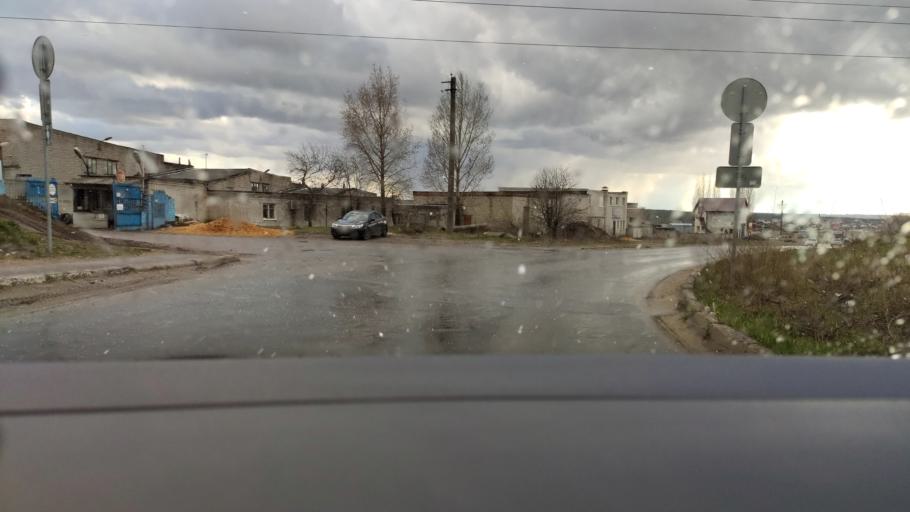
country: RU
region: Voronezj
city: Voronezh
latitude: 51.6394
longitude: 39.1464
